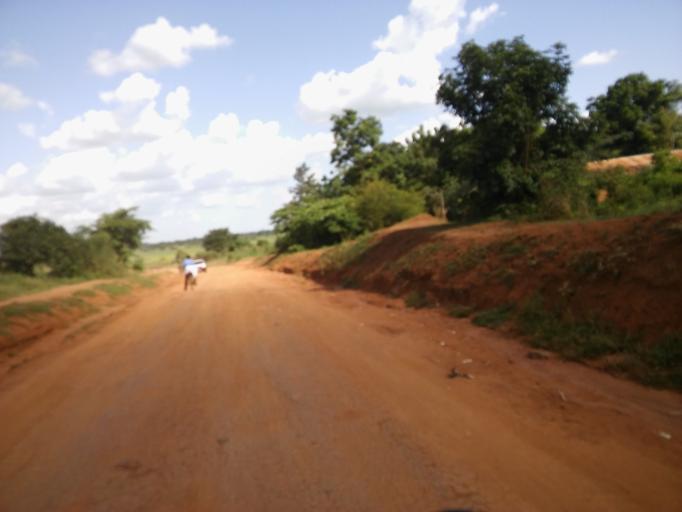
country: UG
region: Eastern Region
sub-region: Pallisa District
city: Pallisa
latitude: 1.1401
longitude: 33.7250
